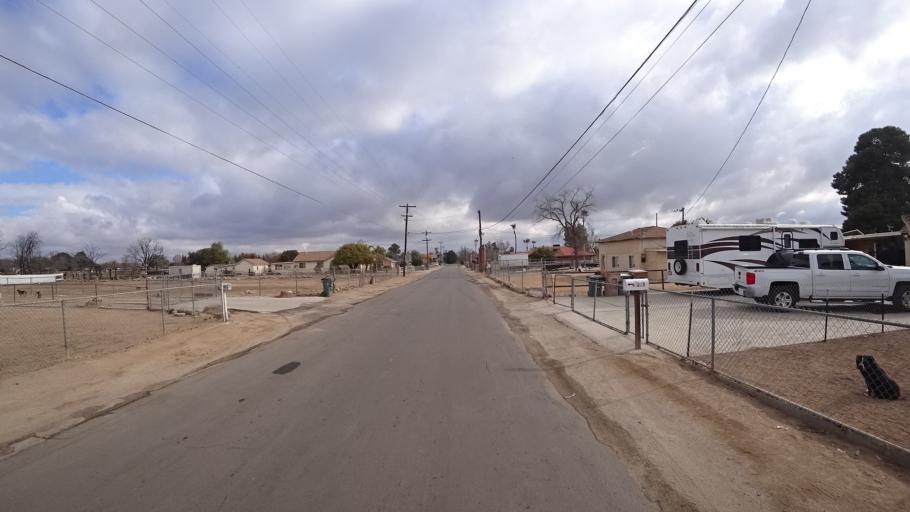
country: US
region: California
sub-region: Kern County
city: Bakersfield
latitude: 35.3367
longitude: -118.9932
